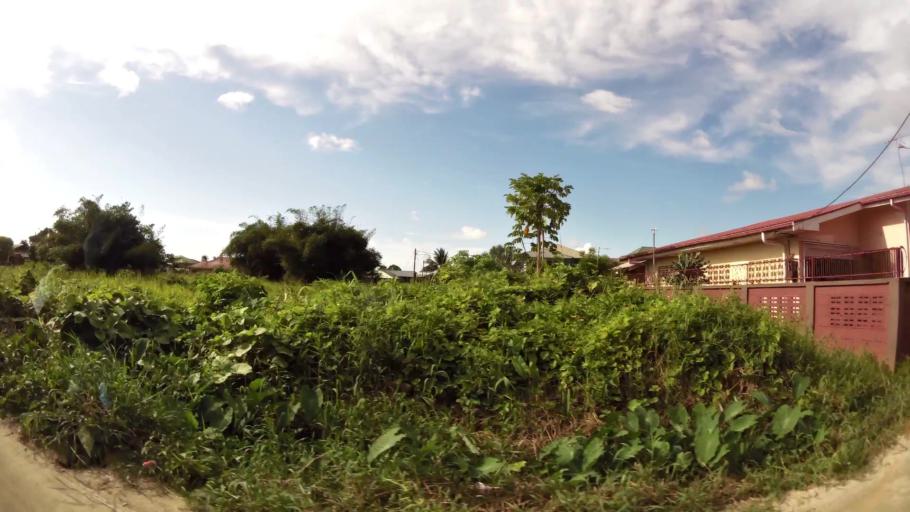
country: SR
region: Paramaribo
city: Paramaribo
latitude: 5.8461
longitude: -55.1822
